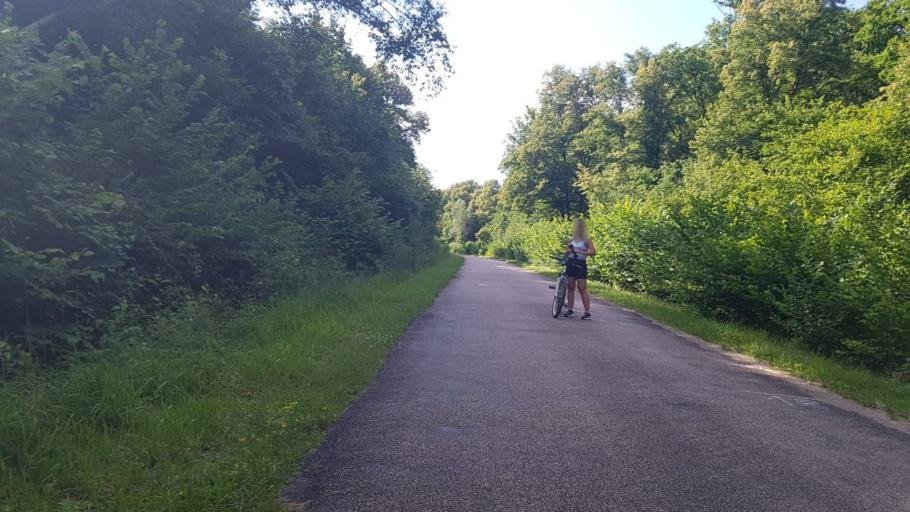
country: FR
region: Picardie
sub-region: Departement de l'Oise
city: Chamant
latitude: 49.1806
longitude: 2.6181
